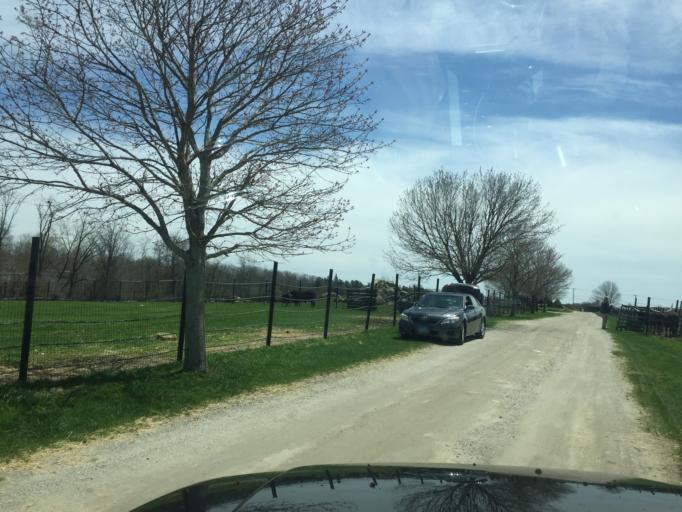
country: US
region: Connecticut
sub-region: Litchfield County
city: West Torrington
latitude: 41.8338
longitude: -73.1952
